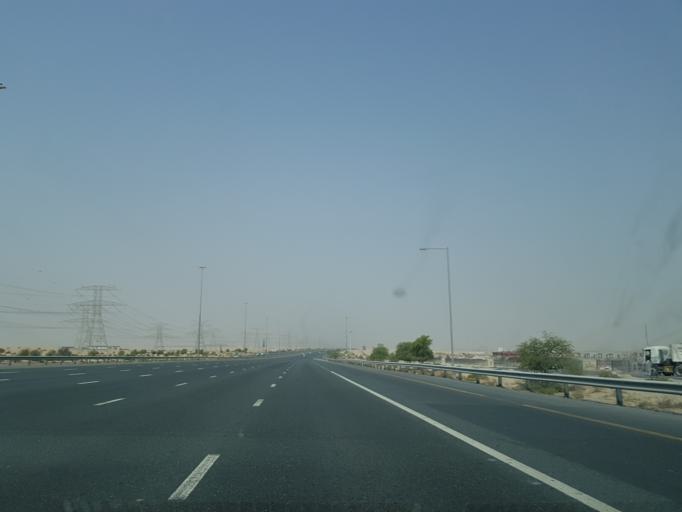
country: AE
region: Dubai
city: Dubai
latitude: 25.0695
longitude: 55.3586
